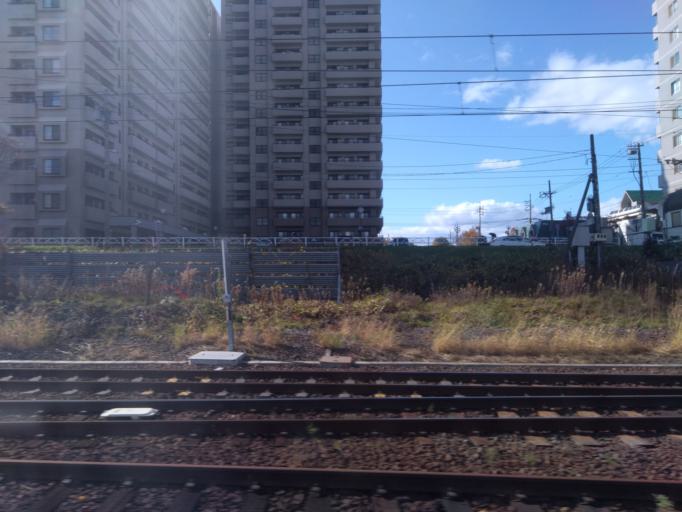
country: JP
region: Hokkaido
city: Kitahiroshima
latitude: 42.9817
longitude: 141.5629
